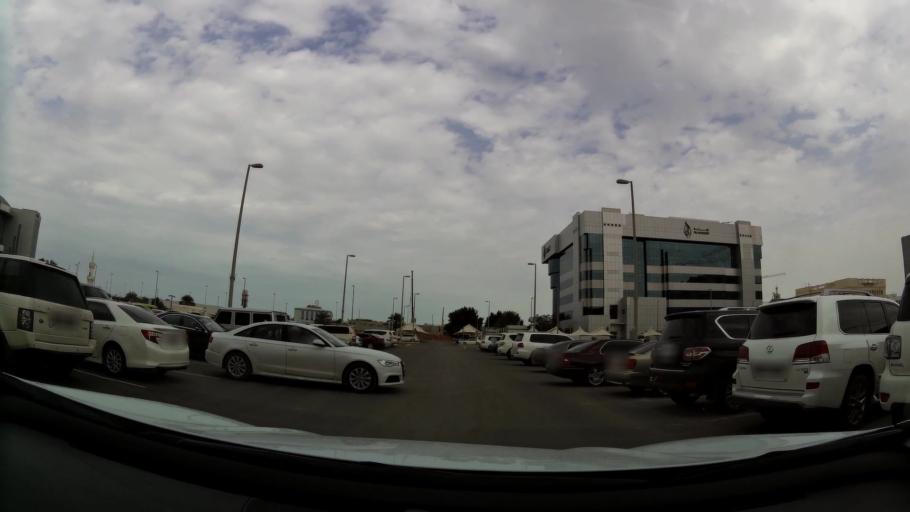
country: AE
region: Abu Dhabi
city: Abu Dhabi
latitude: 24.4218
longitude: 54.4470
